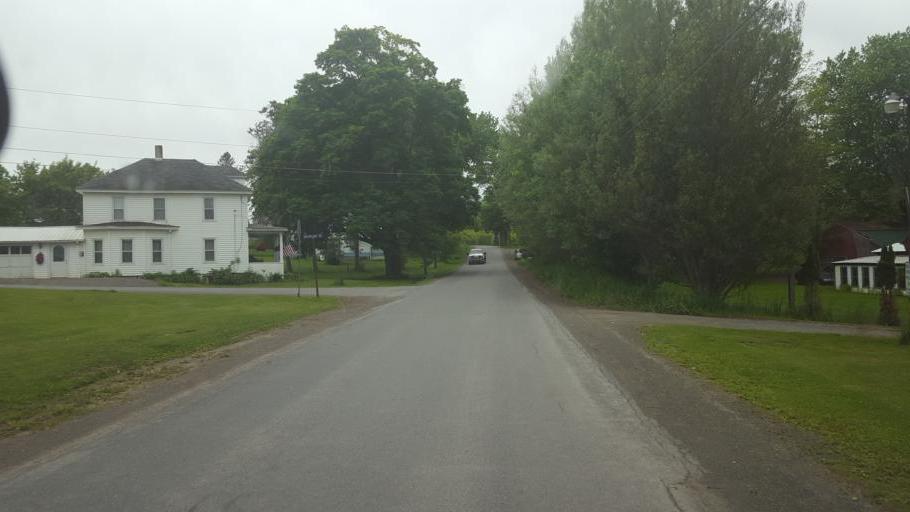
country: US
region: New York
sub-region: Oneida County
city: Waterville
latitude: 42.8426
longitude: -75.2369
